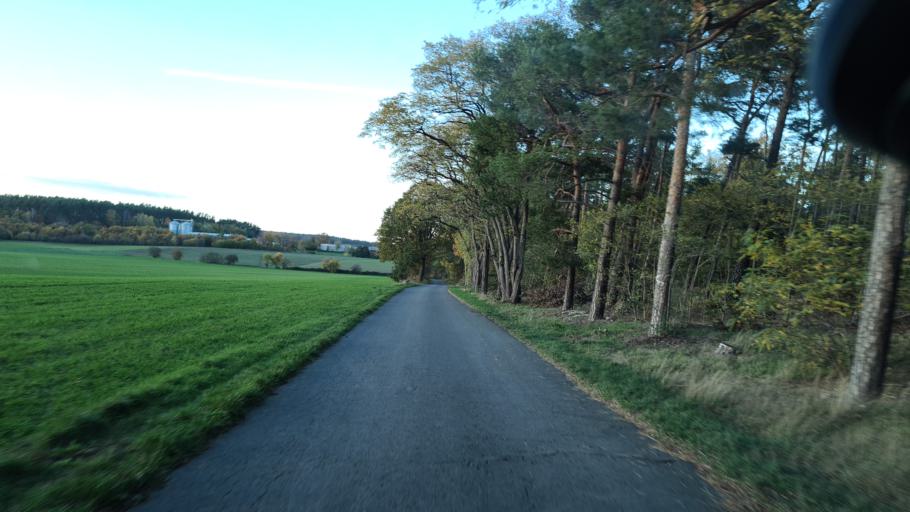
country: DE
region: Saxony
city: Belgern
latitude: 51.4406
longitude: 13.1133
